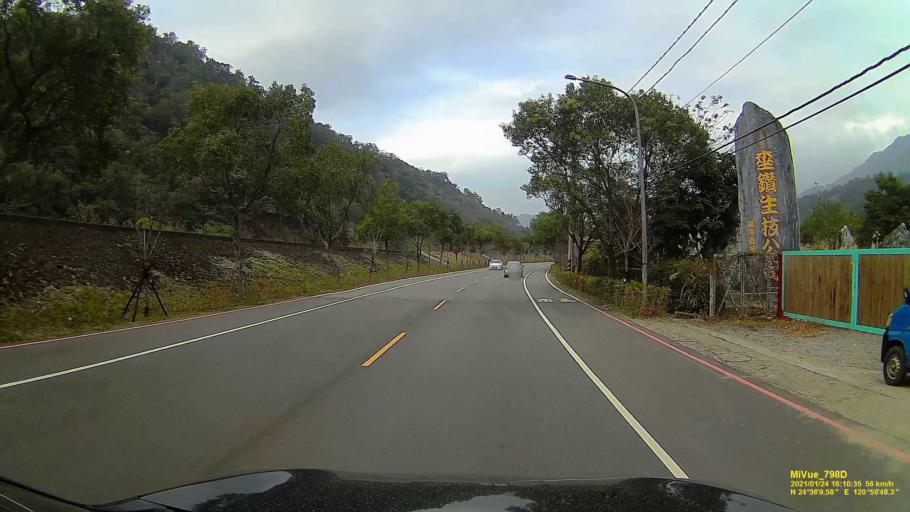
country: TW
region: Taiwan
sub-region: Miaoli
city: Miaoli
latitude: 24.6030
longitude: 120.9969
